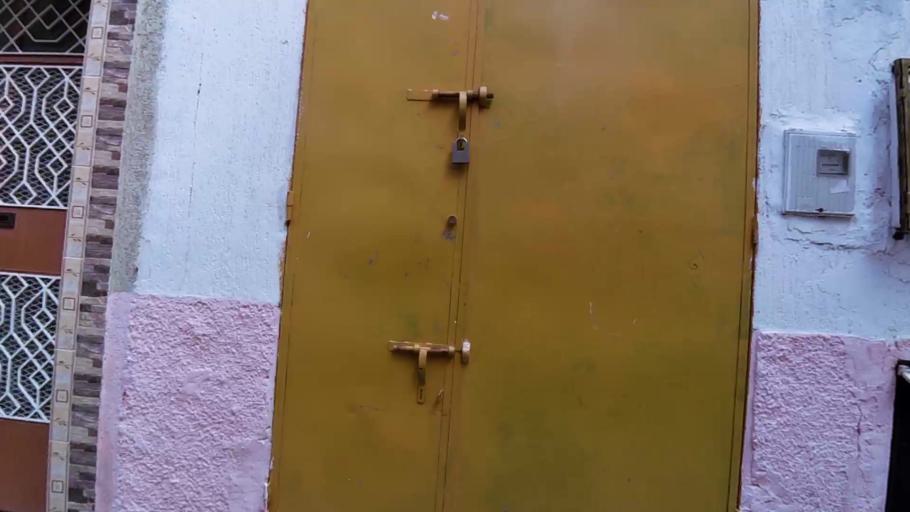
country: MA
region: Tanger-Tetouan
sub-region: Tanger-Assilah
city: Tangier
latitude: 35.7545
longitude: -5.8037
